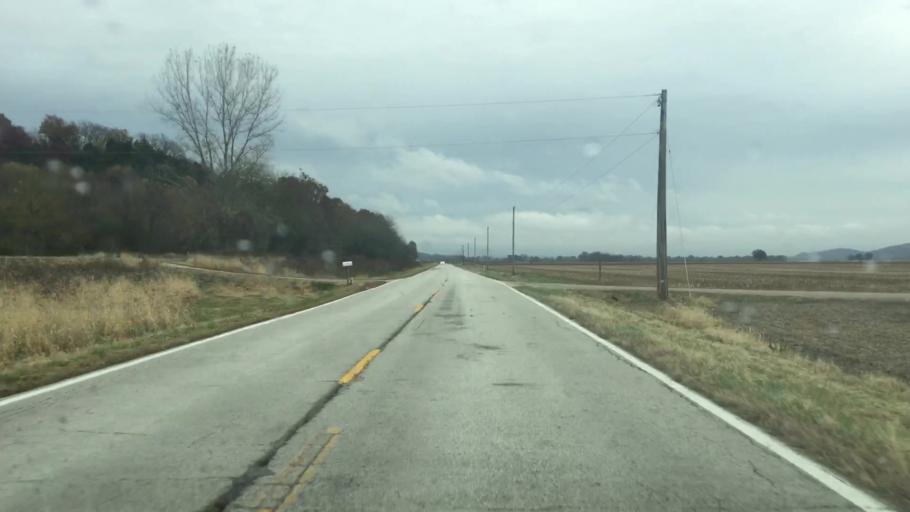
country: US
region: Missouri
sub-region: Gasconade County
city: Hermann
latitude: 38.7063
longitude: -91.5516
